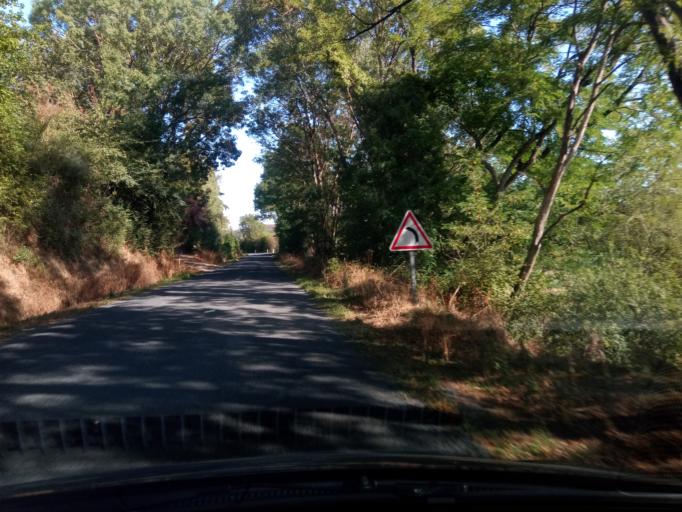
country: FR
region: Poitou-Charentes
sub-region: Departement de la Vienne
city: Saulge
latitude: 46.3704
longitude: 0.8829
